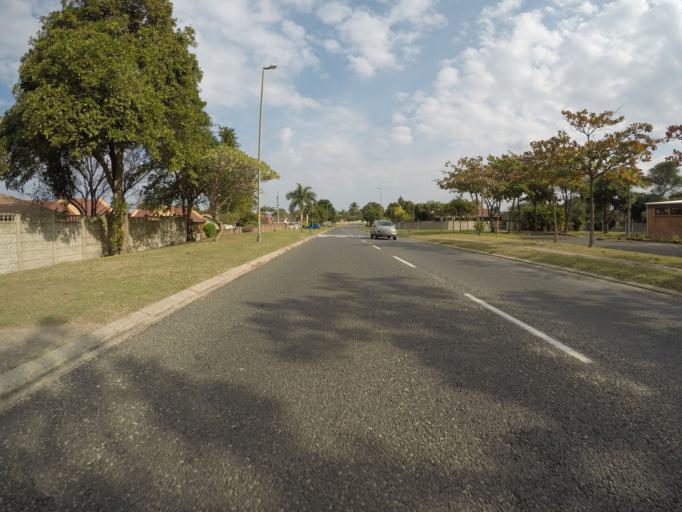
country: ZA
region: KwaZulu-Natal
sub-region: uThungulu District Municipality
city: Richards Bay
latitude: -28.7398
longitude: 32.0650
